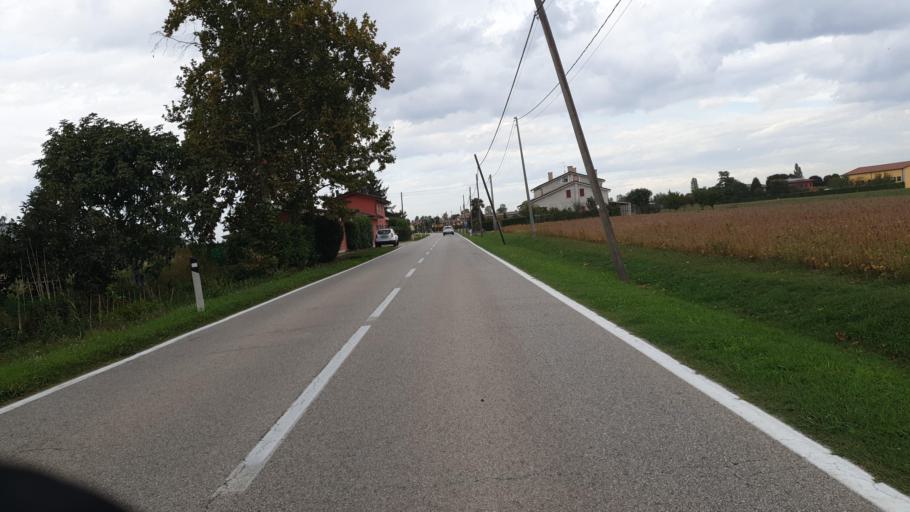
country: IT
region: Veneto
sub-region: Provincia di Padova
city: Bovolenta
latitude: 45.2875
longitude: 11.9431
